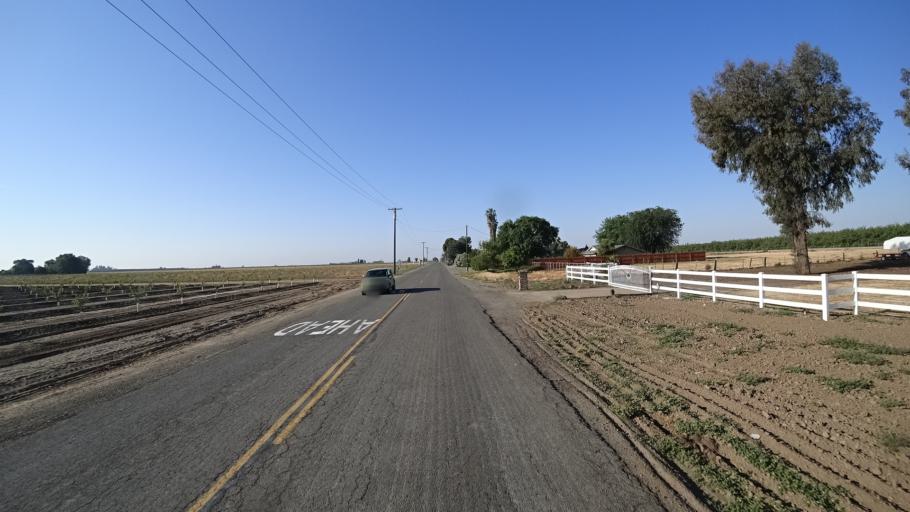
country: US
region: California
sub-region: Kings County
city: Lemoore
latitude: 36.2686
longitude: -119.7449
